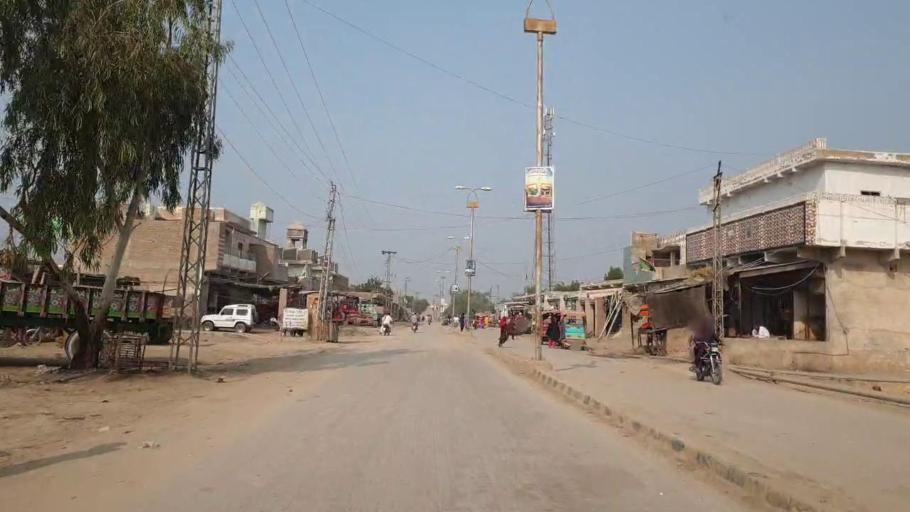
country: PK
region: Sindh
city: Bhan
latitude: 26.5507
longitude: 67.7184
